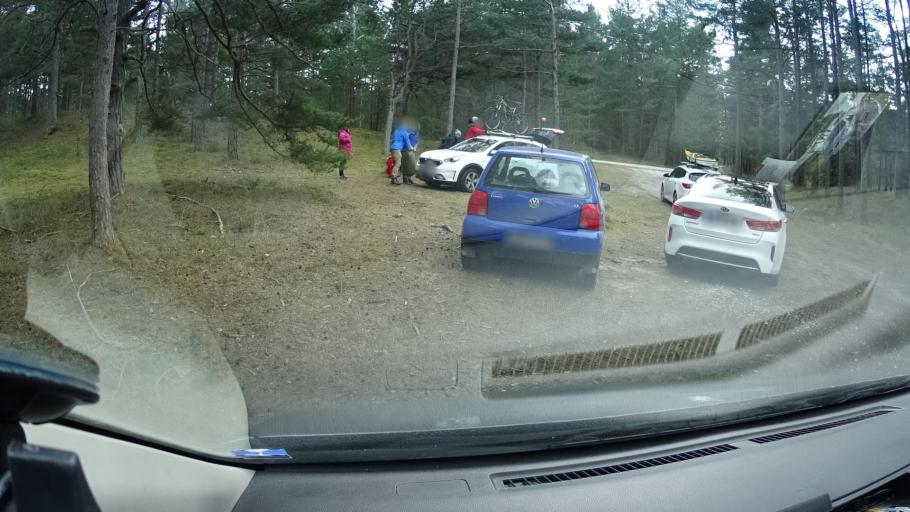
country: SE
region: Gotland
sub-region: Gotland
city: Slite
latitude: 57.9573
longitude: 19.2721
